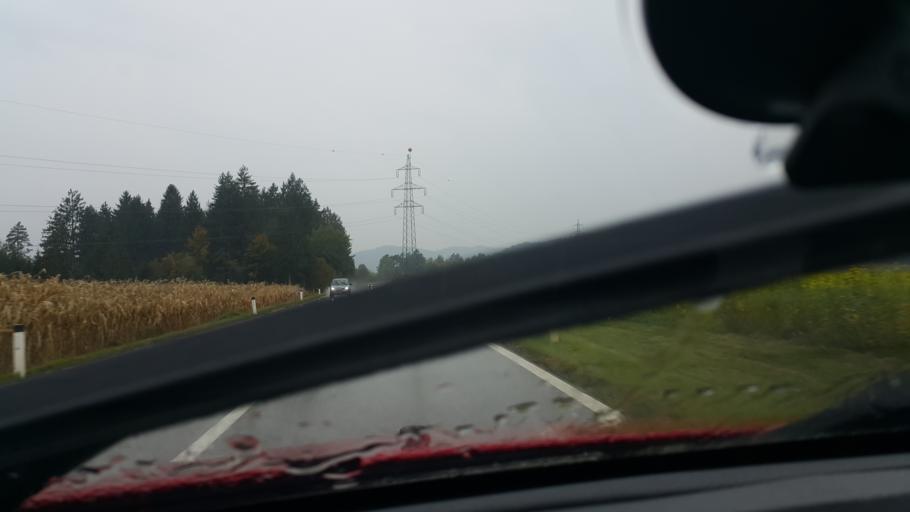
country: AT
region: Carinthia
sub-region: Politischer Bezirk Volkermarkt
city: Ruden
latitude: 46.6476
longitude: 14.8062
